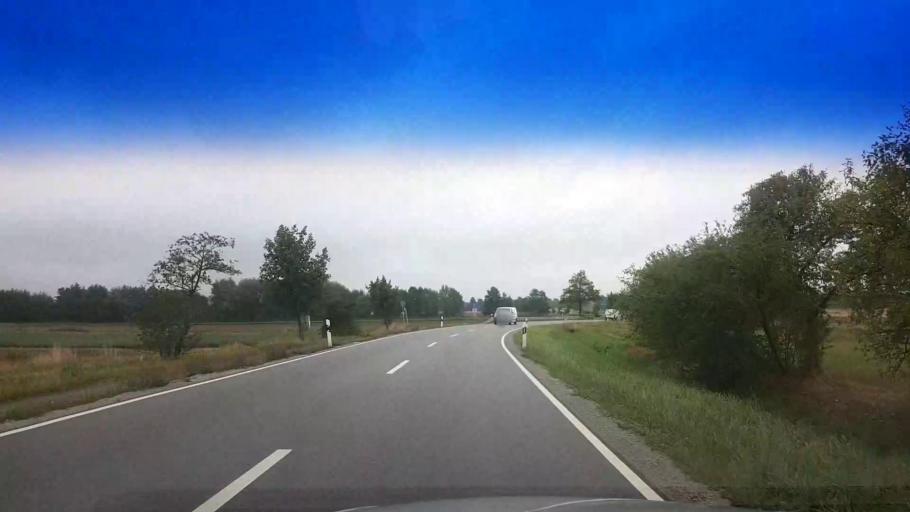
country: DE
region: Bavaria
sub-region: Upper Franconia
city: Eggolsheim
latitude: 49.7823
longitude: 11.0494
